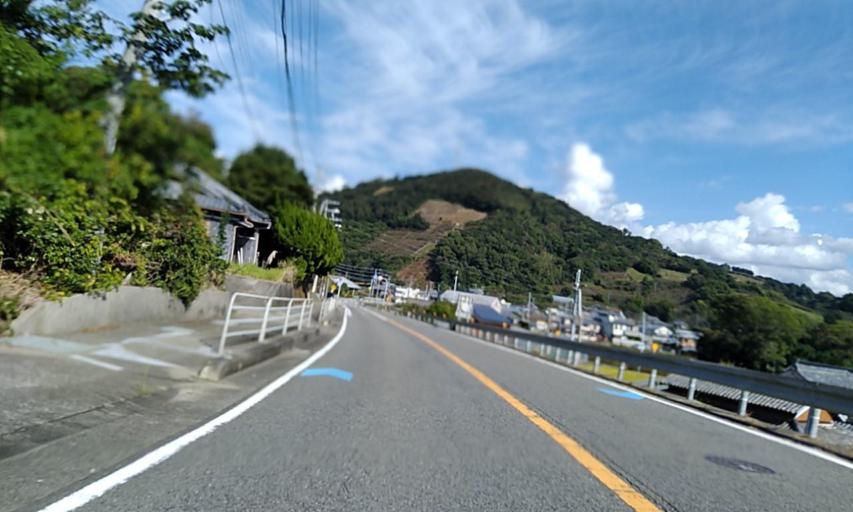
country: JP
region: Wakayama
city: Tanabe
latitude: 33.7823
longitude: 135.2832
